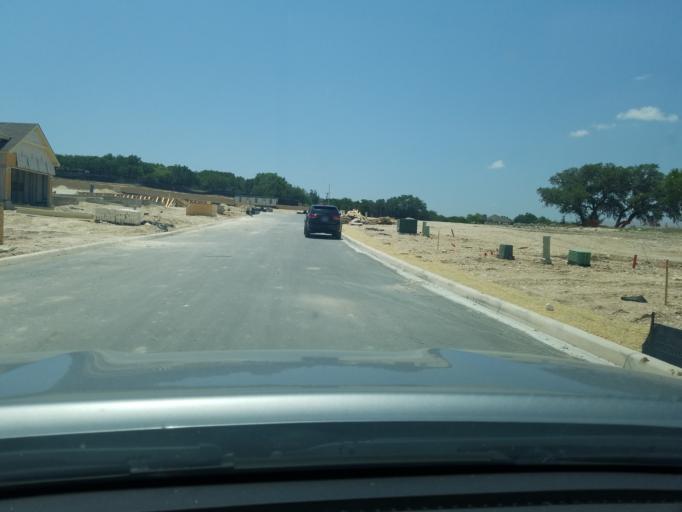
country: US
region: Texas
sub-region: Bexar County
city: Timberwood Park
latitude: 29.7063
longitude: -98.4996
